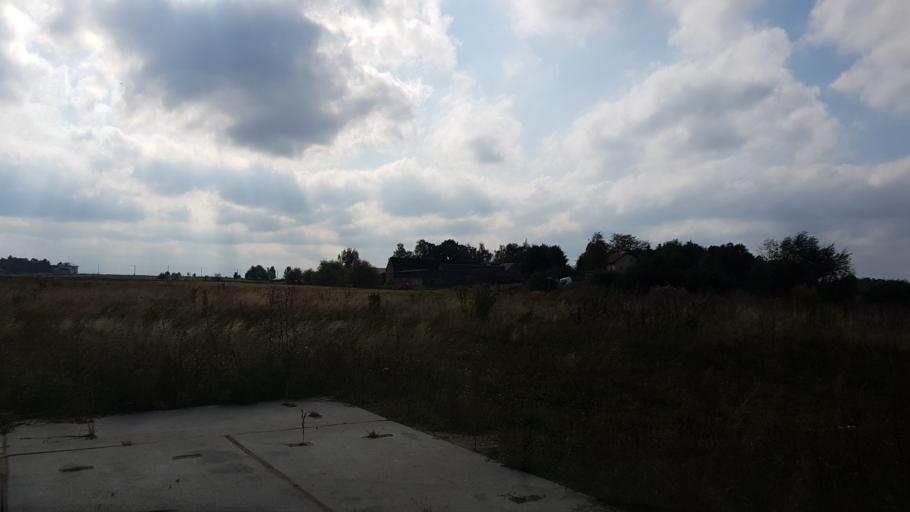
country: PL
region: West Pomeranian Voivodeship
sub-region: Koszalin
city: Koszalin
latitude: 54.1768
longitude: 16.1548
